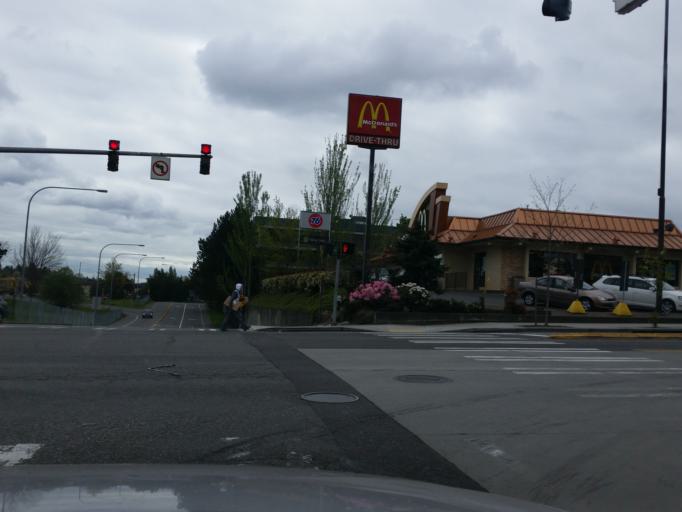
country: US
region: Washington
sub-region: King County
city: Shoreline
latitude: 47.7088
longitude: -122.3314
